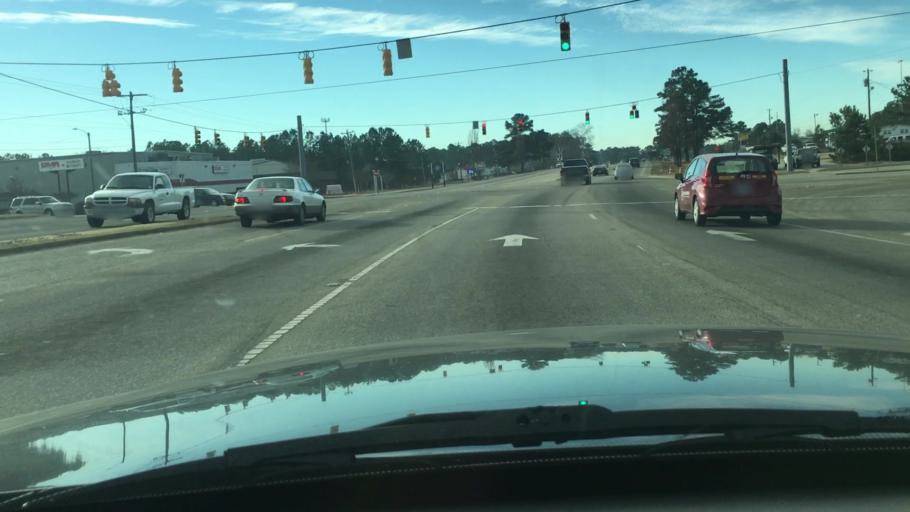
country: US
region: North Carolina
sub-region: Cumberland County
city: Hope Mills
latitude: 35.0009
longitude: -78.8995
